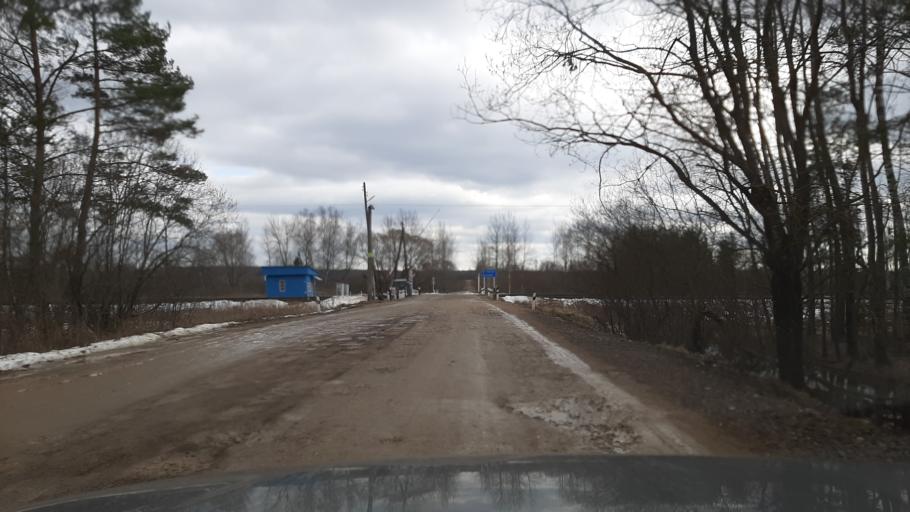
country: RU
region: Ivanovo
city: Teykovo
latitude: 56.8832
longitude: 40.6227
